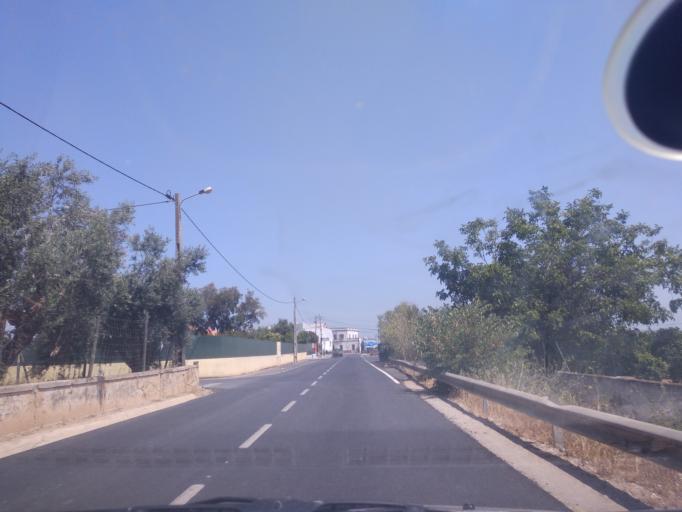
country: PT
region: Faro
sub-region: Faro
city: Faro
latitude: 37.0510
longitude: -7.9394
